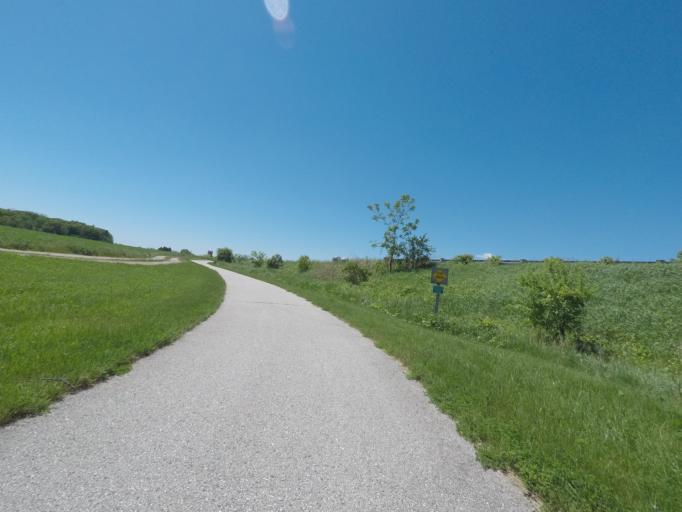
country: US
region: Wisconsin
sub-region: Sheboygan County
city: Kohler
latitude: 43.7503
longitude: -87.7998
